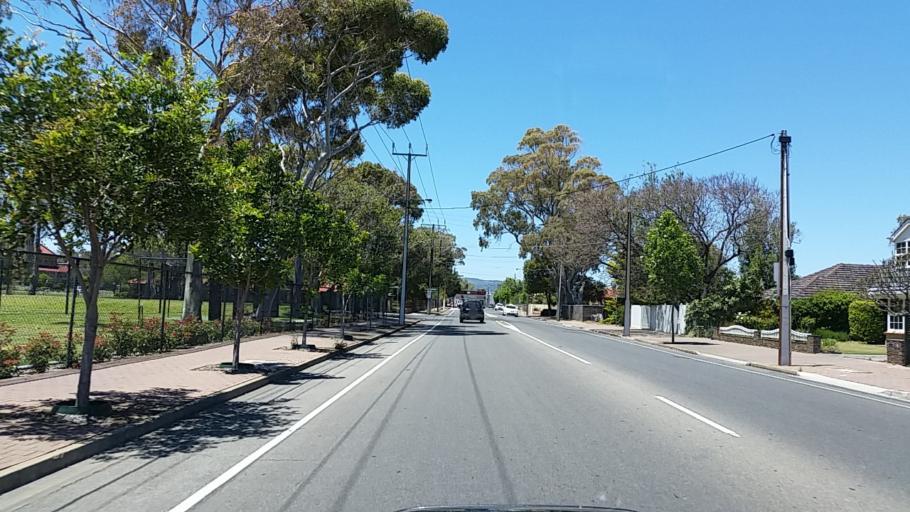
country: AU
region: South Australia
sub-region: Holdfast Bay
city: North Brighton
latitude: -34.9968
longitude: 138.5184
